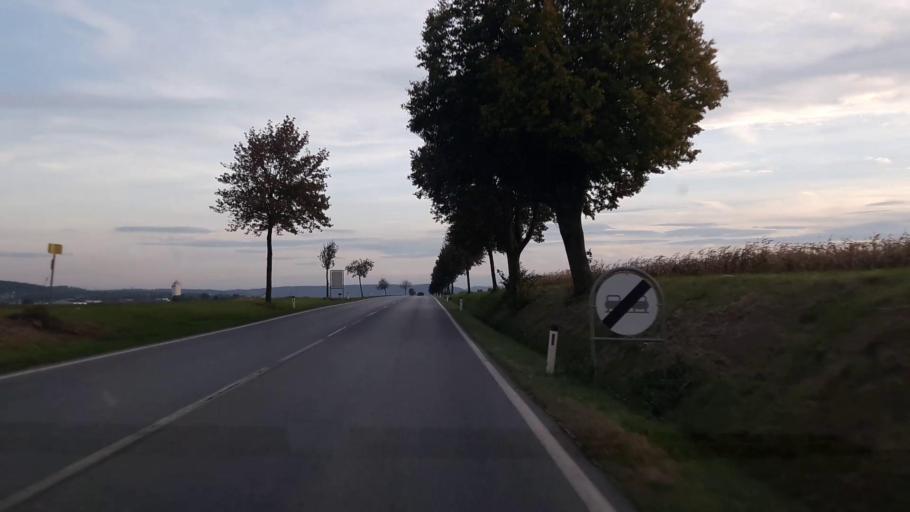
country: AT
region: Lower Austria
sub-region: Politischer Bezirk Korneuburg
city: Harmannsdorf
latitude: 48.4073
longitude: 16.3775
